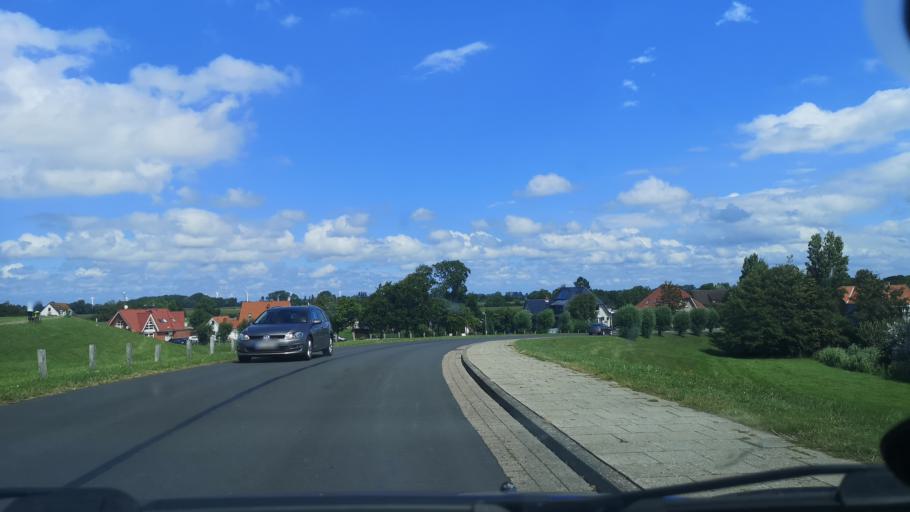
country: DE
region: Lower Saxony
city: Wremen
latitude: 53.6473
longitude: 8.4956
